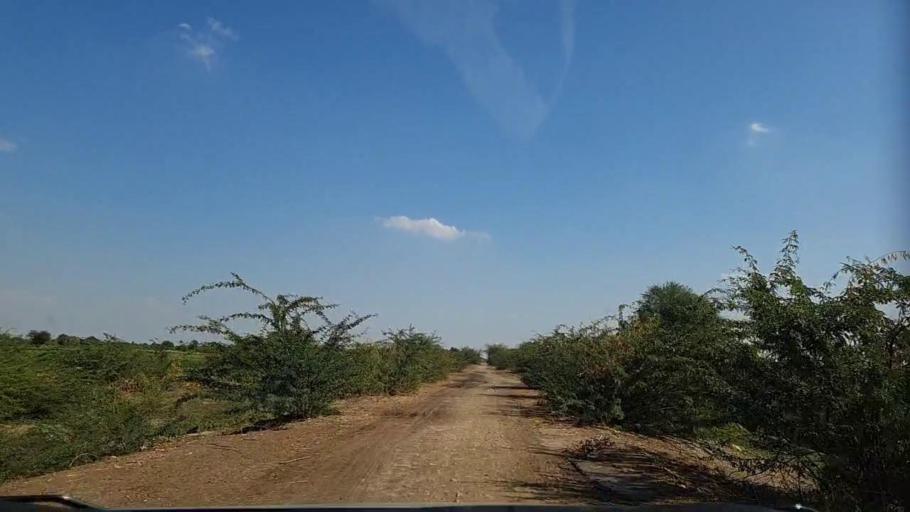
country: PK
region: Sindh
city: Pithoro
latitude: 25.6898
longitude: 69.3878
